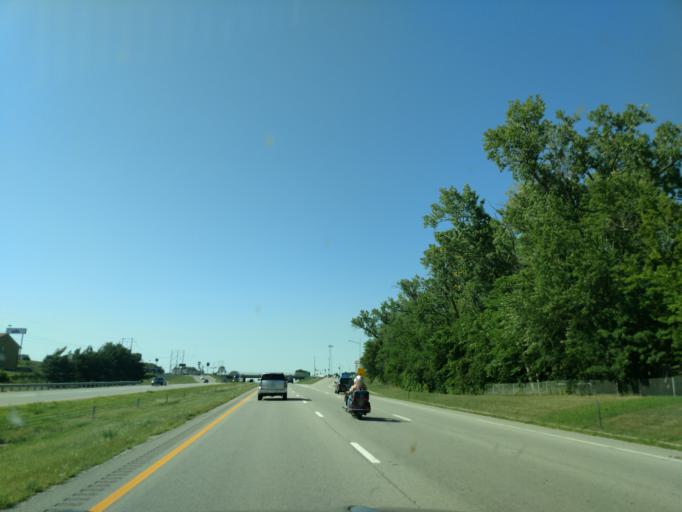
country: US
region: Missouri
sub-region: Buchanan County
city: Saint Joseph
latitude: 39.7731
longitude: -94.7930
